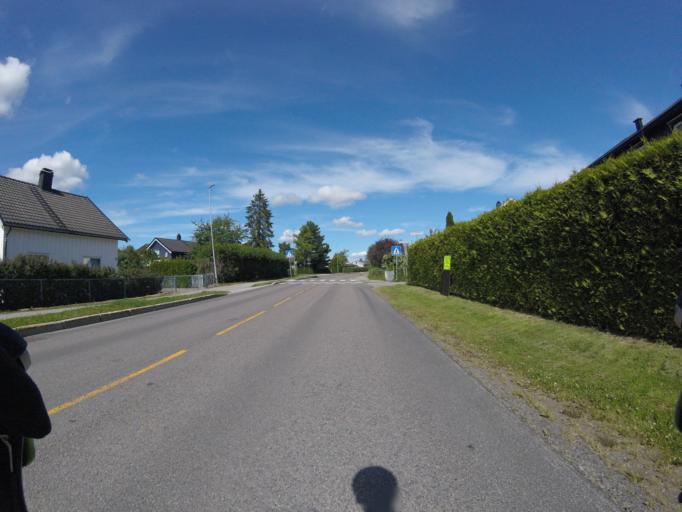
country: NO
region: Akershus
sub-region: Skedsmo
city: Lillestrom
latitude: 59.9424
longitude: 11.0156
